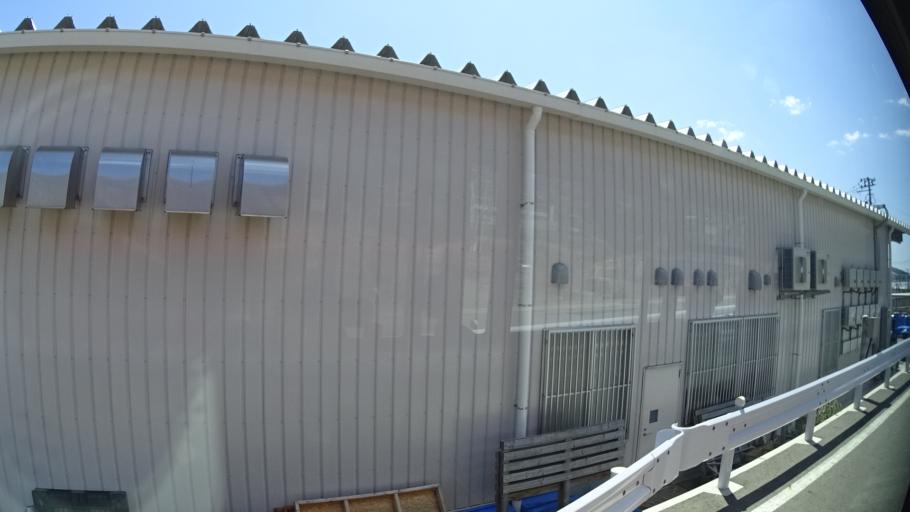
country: JP
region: Iwate
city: Ofunato
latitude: 39.0582
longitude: 141.7209
